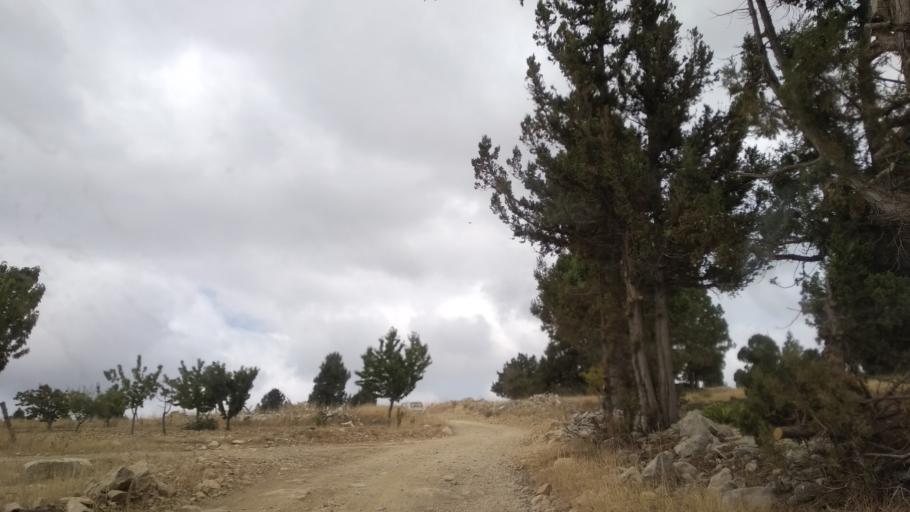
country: TR
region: Mersin
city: Sarikavak
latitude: 36.5656
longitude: 33.7668
